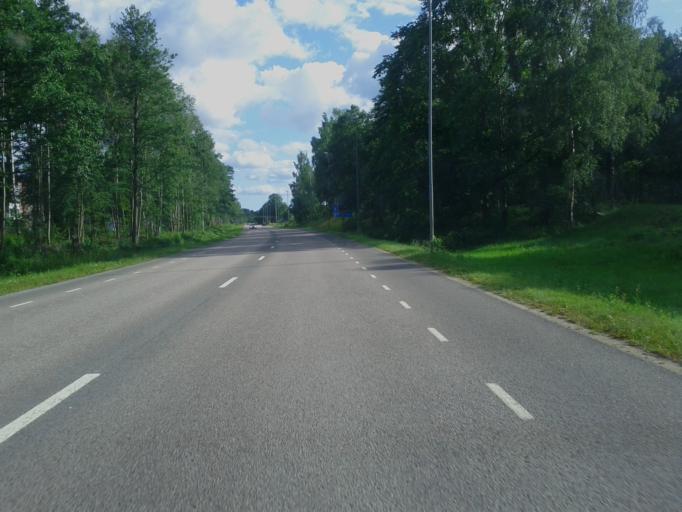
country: SE
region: Vaestmanland
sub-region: Sala Kommun
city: Sala
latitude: 59.9179
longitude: 16.5862
